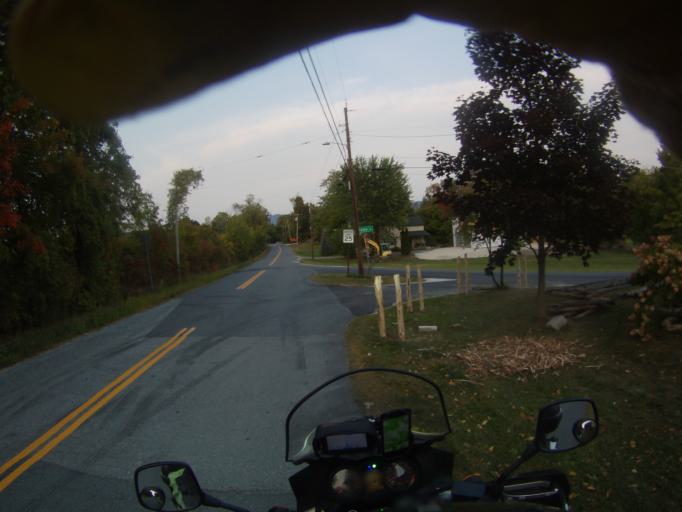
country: US
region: Vermont
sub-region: Rutland County
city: Brandon
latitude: 43.7940
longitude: -73.0989
